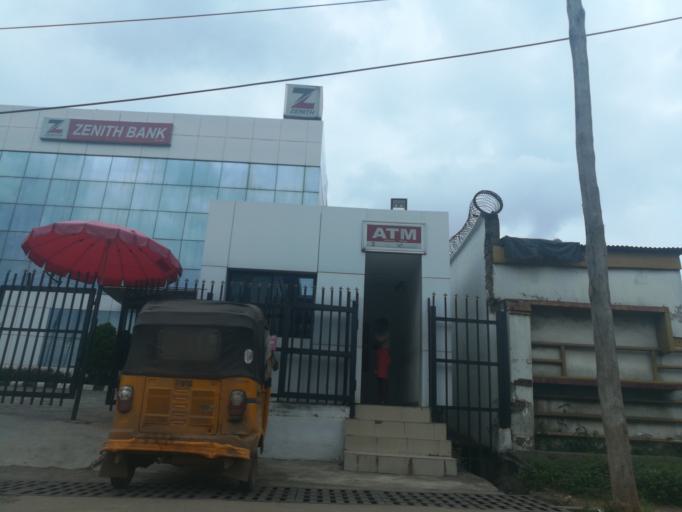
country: NG
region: Lagos
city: Ikeja
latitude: 6.6079
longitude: 3.3483
